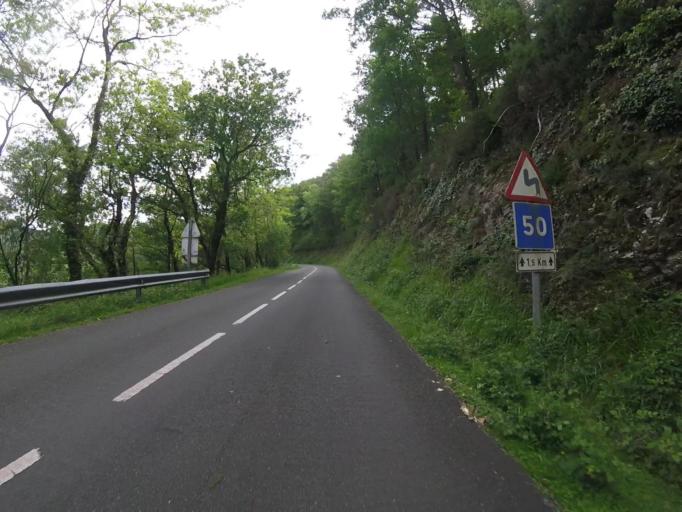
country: ES
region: Basque Country
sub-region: Provincia de Guipuzcoa
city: Errenteria
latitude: 43.2591
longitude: -1.8497
